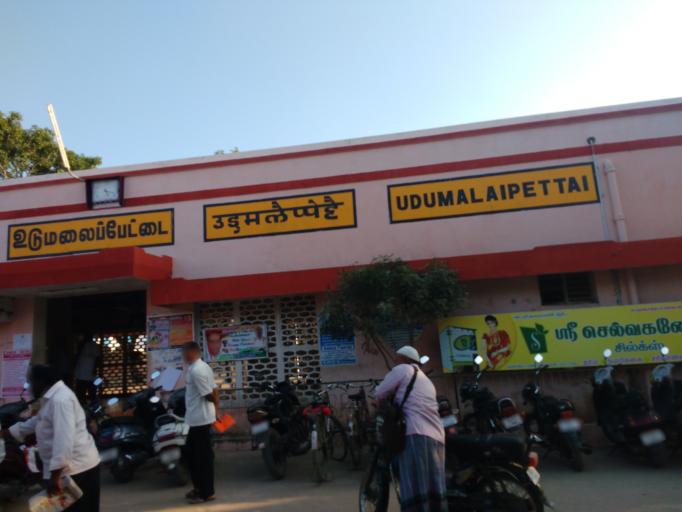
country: IN
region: Tamil Nadu
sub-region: Tiruppur
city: Udumalaippettai
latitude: 10.5793
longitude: 77.2500
